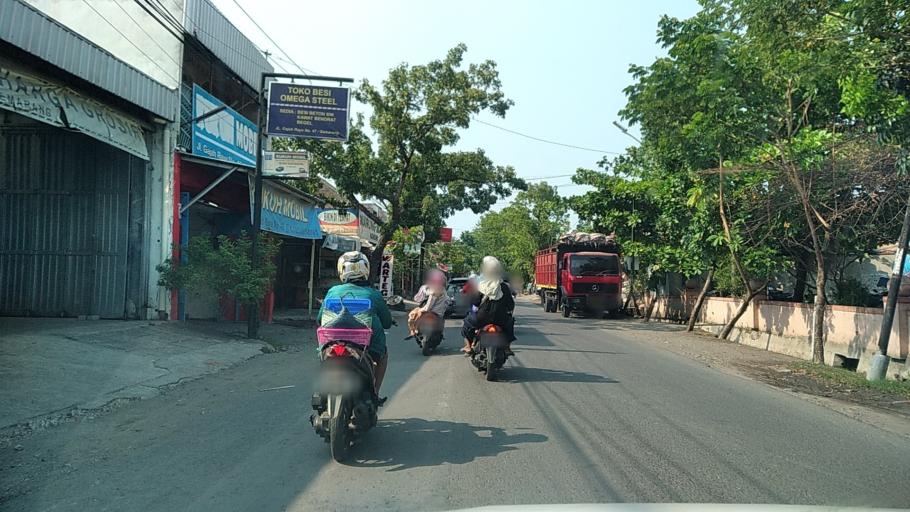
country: ID
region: Central Java
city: Semarang
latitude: -6.9807
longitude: 110.4490
